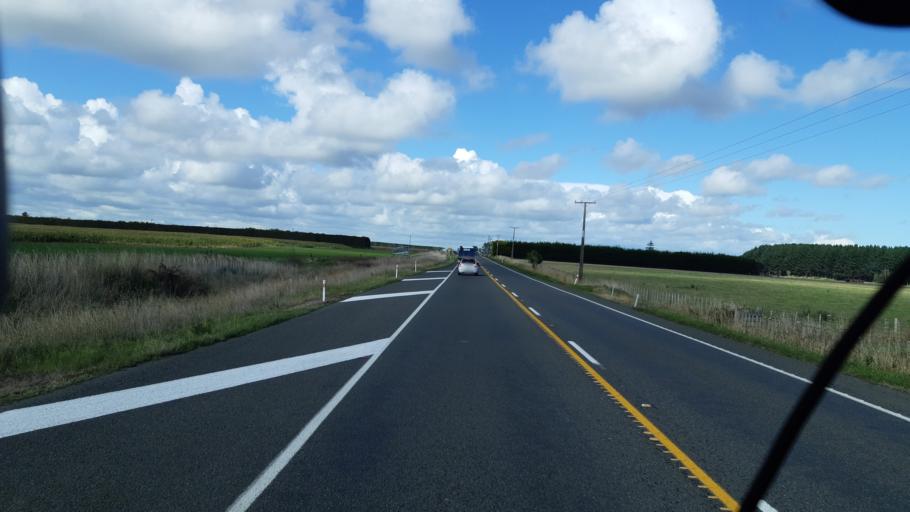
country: NZ
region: Manawatu-Wanganui
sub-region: Wanganui District
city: Wanganui
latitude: -39.9871
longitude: 175.1574
